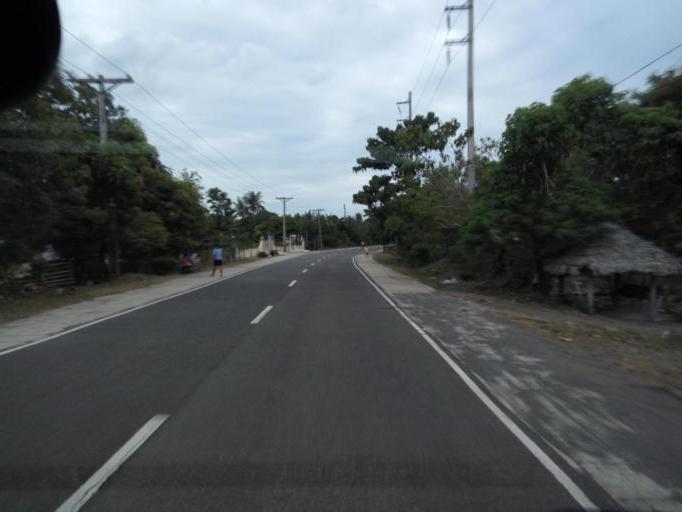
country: PH
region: Cagayan Valley
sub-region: Province of Cagayan
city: Casambalangan
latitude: 18.4004
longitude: 122.1255
